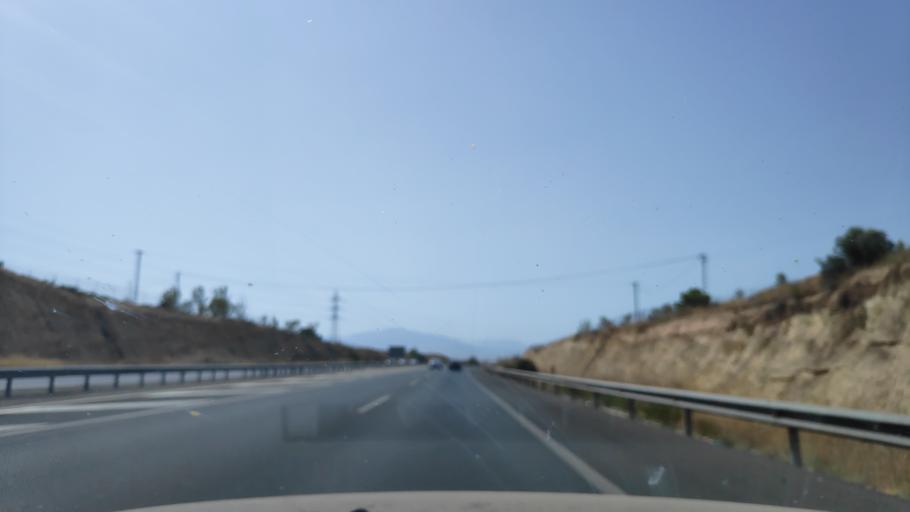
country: ES
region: Murcia
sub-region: Murcia
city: Molina de Segura
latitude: 38.0469
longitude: -1.1692
